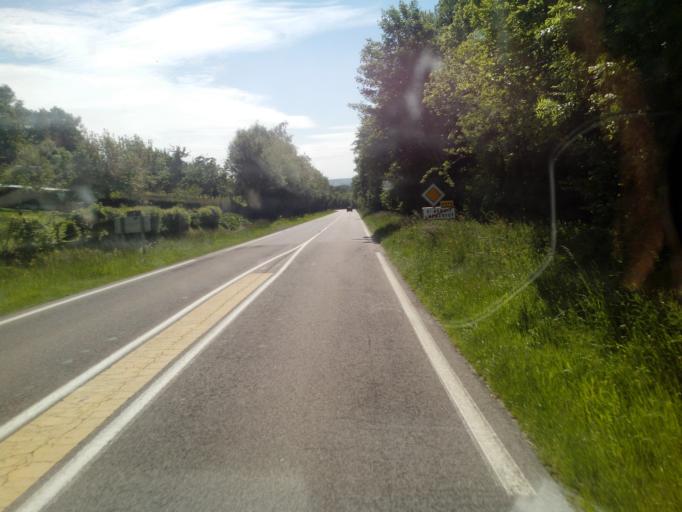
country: FR
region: Lower Normandy
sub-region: Departement du Calvados
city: Ablon
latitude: 49.3174
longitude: 0.2659
